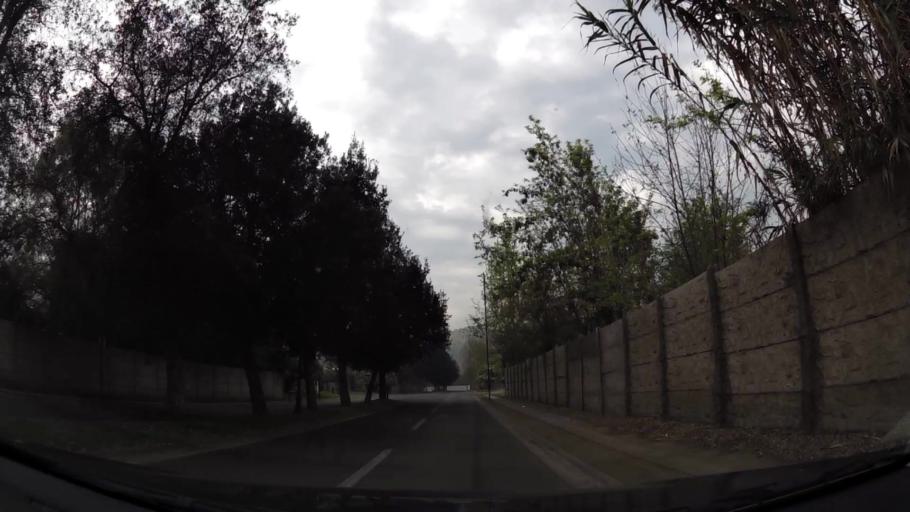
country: CL
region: Santiago Metropolitan
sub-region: Provincia de Chacabuco
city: Chicureo Abajo
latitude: -33.2451
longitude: -70.6776
